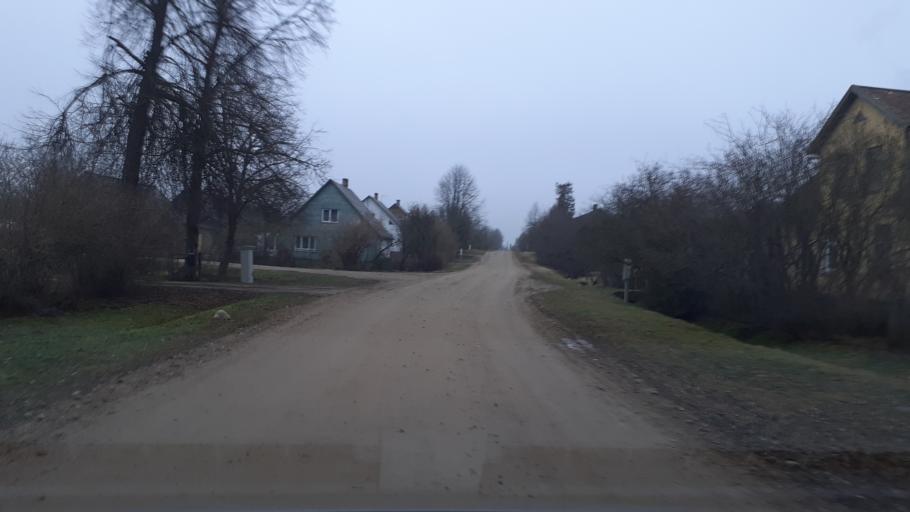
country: LV
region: Talsu Rajons
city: Sabile
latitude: 56.9531
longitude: 22.3995
